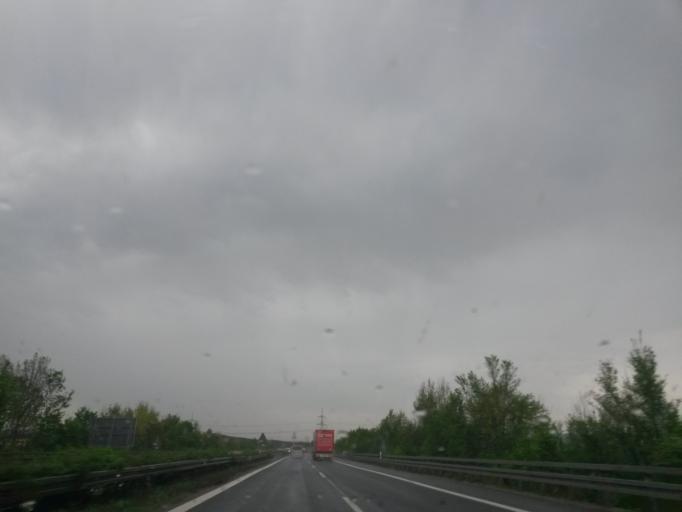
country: DE
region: Bavaria
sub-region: Upper Franconia
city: Forchheim
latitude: 49.7050
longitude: 11.0584
